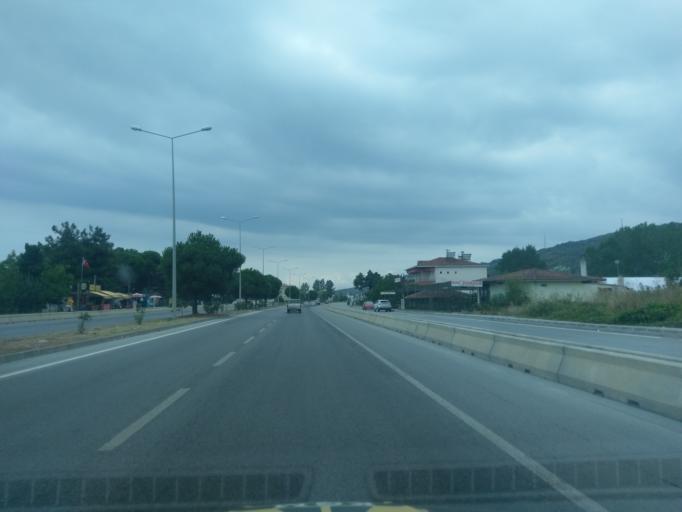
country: TR
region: Samsun
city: Taflan
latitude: 41.3966
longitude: 36.1967
